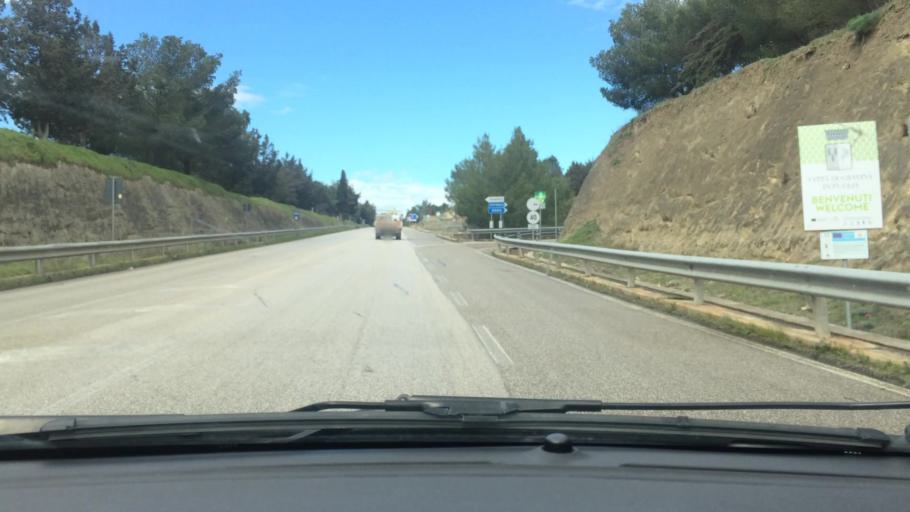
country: IT
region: Apulia
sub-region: Provincia di Bari
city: Gravina in Puglia
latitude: 40.8055
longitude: 16.4196
